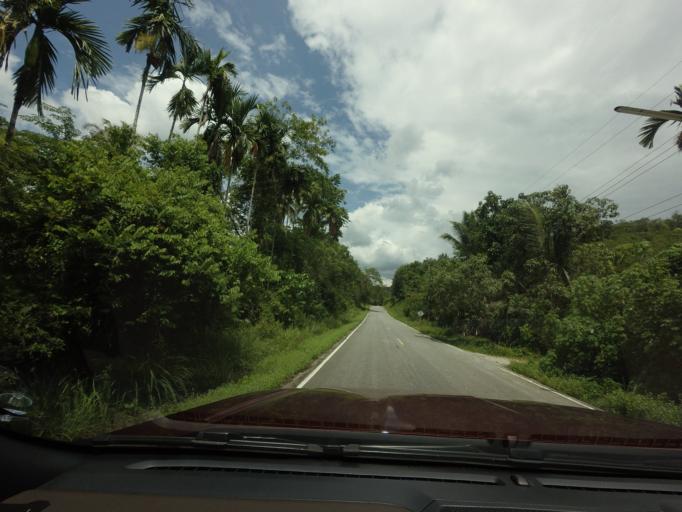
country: TH
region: Narathiwat
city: Chanae
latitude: 6.0495
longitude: 101.6887
